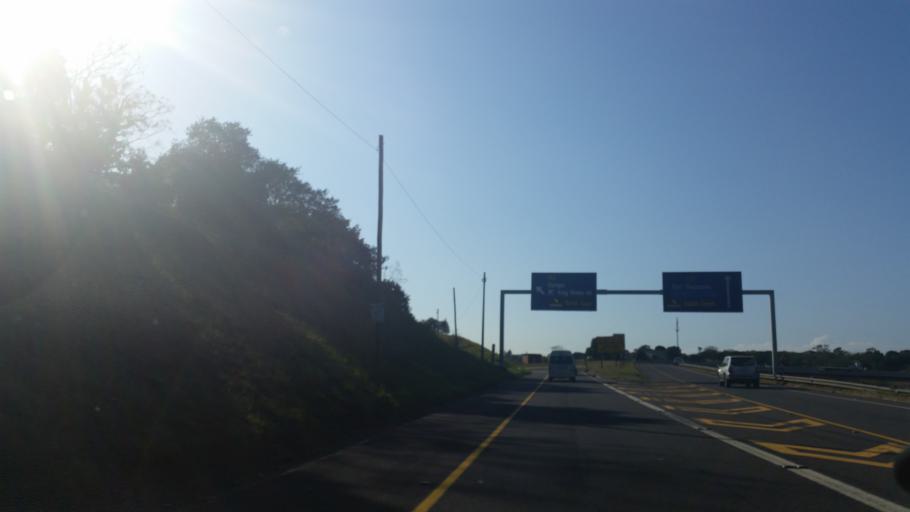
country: ZA
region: KwaZulu-Natal
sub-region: eThekwini Metropolitan Municipality
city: Berea
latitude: -29.8403
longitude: 30.9544
